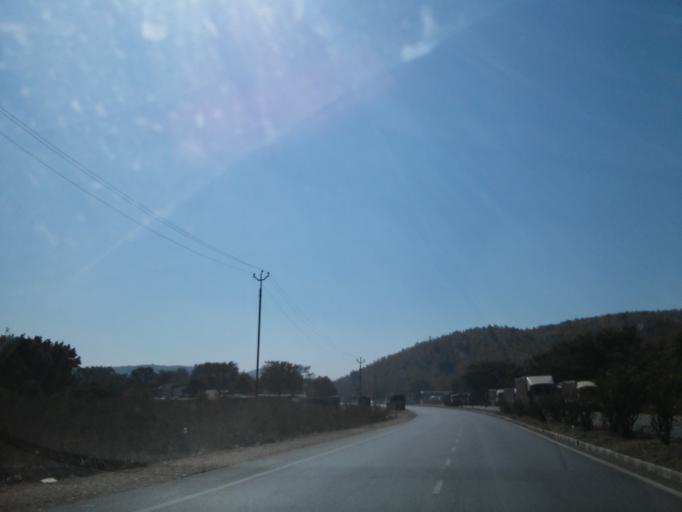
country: IN
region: Gujarat
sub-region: Sabar Kantha
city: Meghraj
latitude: 23.7116
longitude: 73.3910
